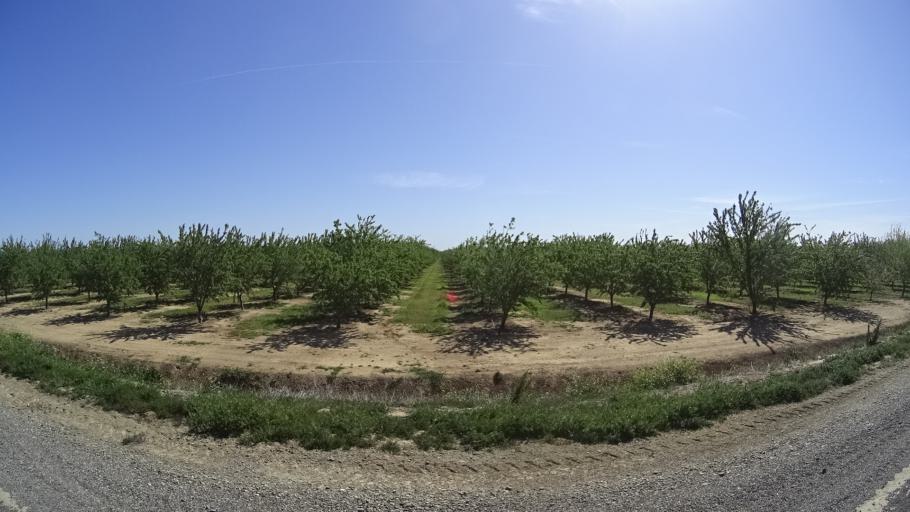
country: US
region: California
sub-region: Glenn County
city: Hamilton City
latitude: 39.6394
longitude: -122.1039
